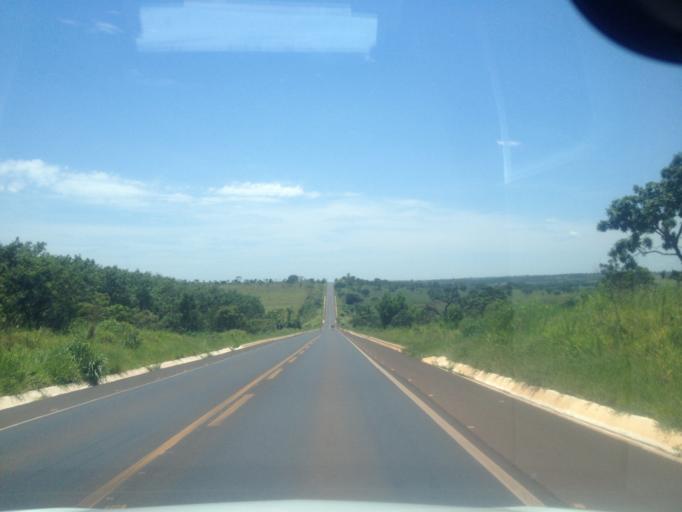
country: BR
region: Minas Gerais
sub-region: Monte Alegre De Minas
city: Monte Alegre de Minas
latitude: -18.8794
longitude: -49.0996
